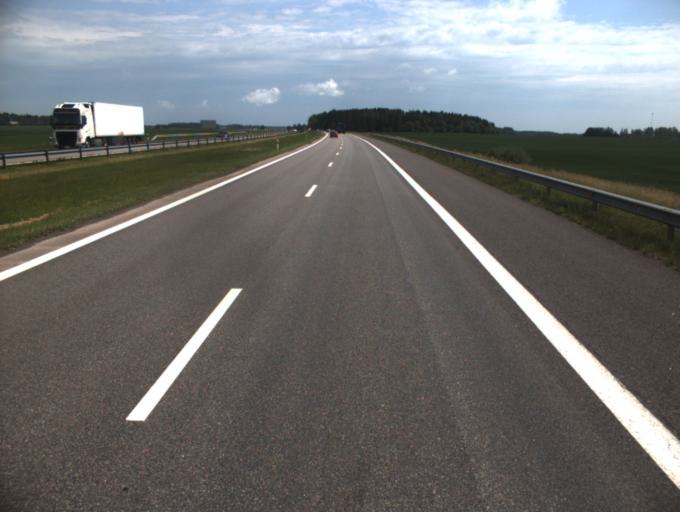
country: LT
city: Ariogala
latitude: 55.2860
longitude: 23.3011
